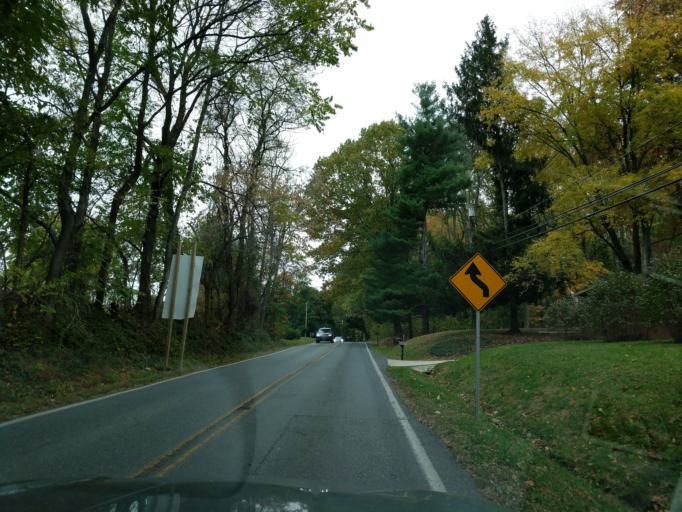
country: US
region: Maryland
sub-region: Frederick County
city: Spring Ridge
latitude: 39.4108
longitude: -77.2988
